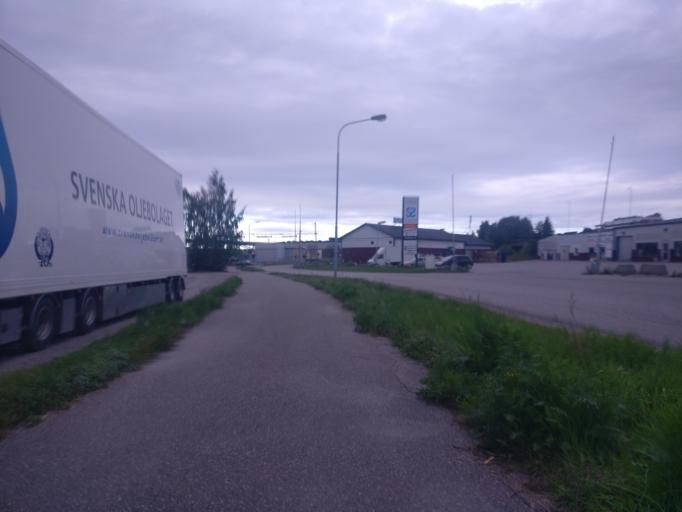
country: SE
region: Vaesternorrland
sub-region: Sundsvalls Kommun
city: Sundsvall
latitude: 62.3864
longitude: 17.3259
